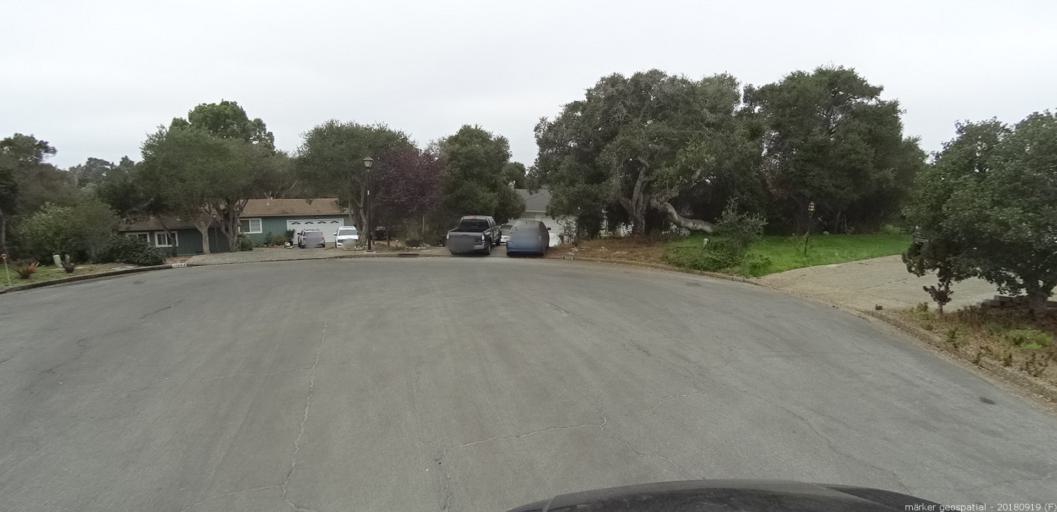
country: US
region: California
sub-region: Monterey County
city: Prunedale
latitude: 36.7792
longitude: -121.7129
